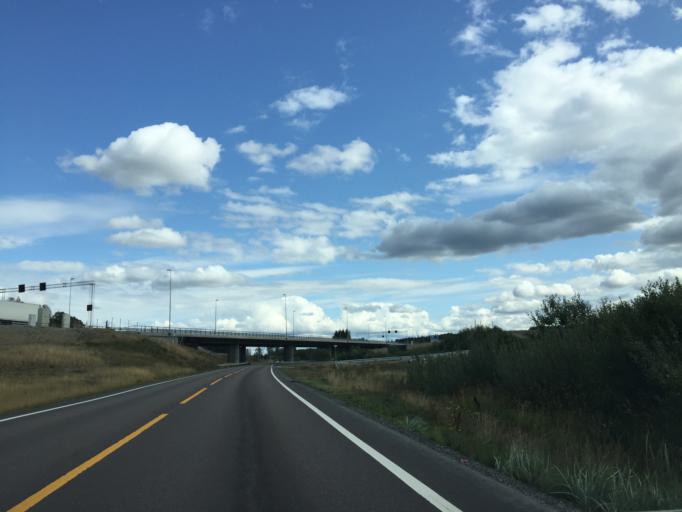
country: NO
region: Ostfold
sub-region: Hobol
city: Tomter
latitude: 59.6225
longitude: 10.9939
